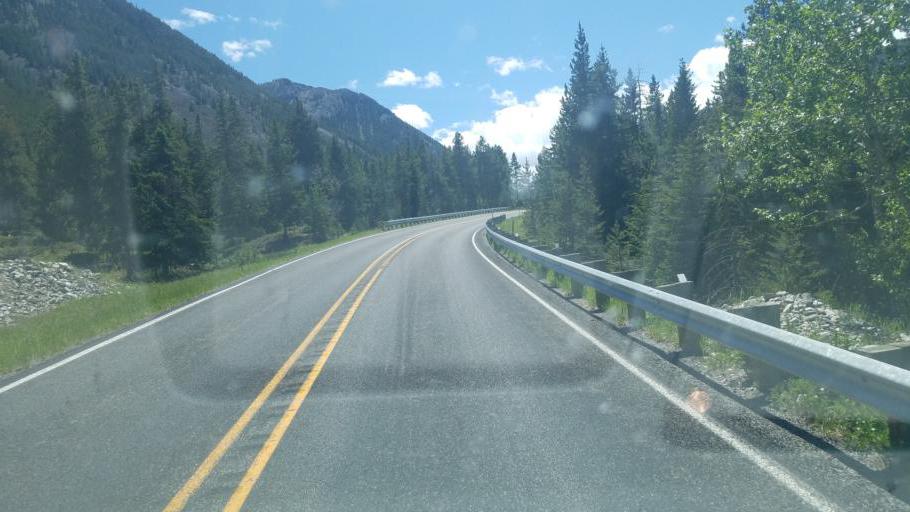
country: US
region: Montana
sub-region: Carbon County
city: Red Lodge
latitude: 45.0663
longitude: -109.3941
